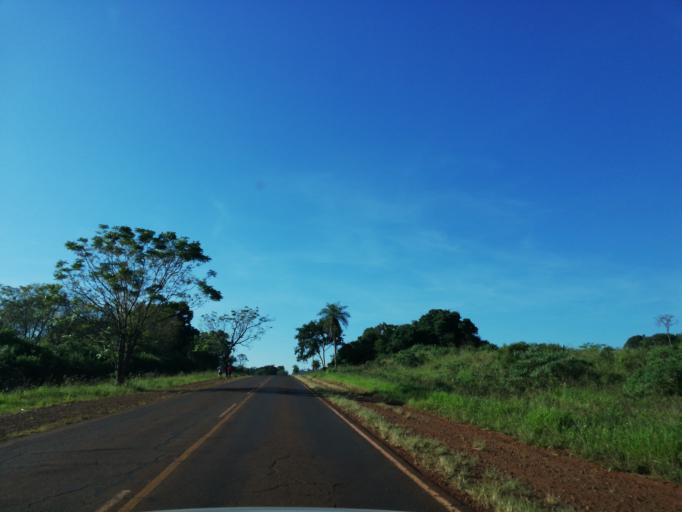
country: AR
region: Misiones
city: Gobernador Roca
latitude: -27.1862
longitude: -55.4479
